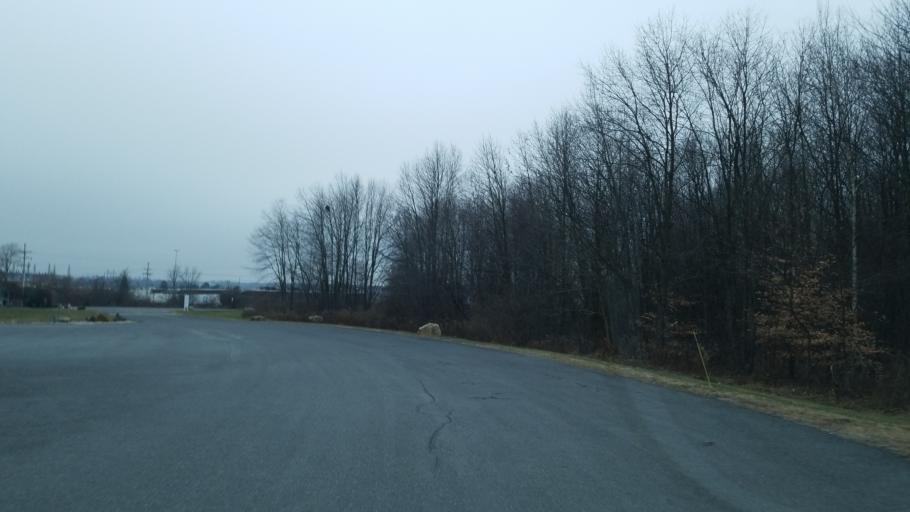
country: US
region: Pennsylvania
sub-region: Clearfield County
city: DuBois
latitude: 41.1167
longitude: -78.7276
